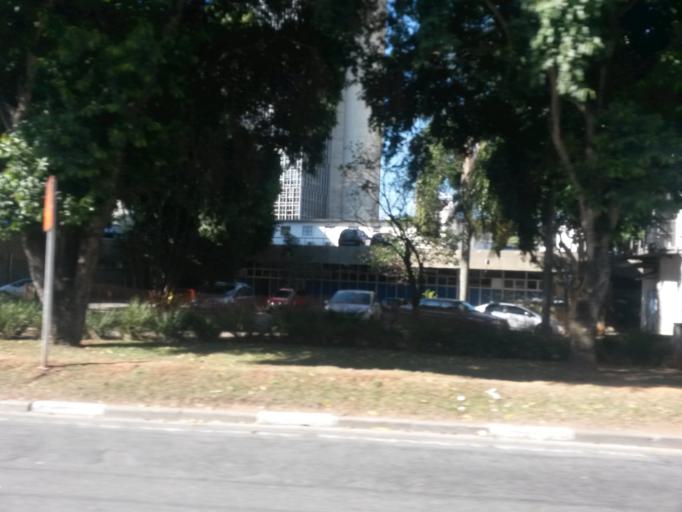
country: BR
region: Sao Paulo
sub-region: Sao Bernardo Do Campo
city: Sao Bernardo do Campo
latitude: -23.6960
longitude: -46.5527
